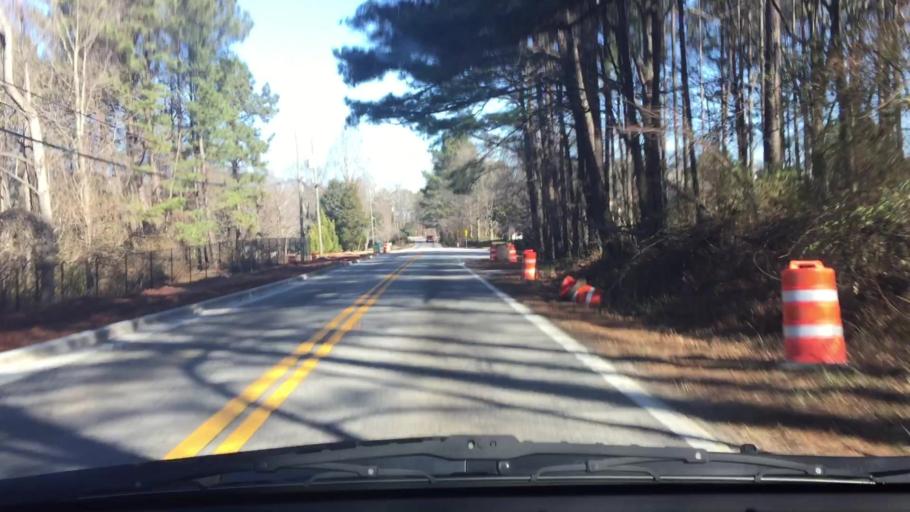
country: US
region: Georgia
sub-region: Clayton County
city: Conley
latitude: 33.6365
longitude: -84.2834
